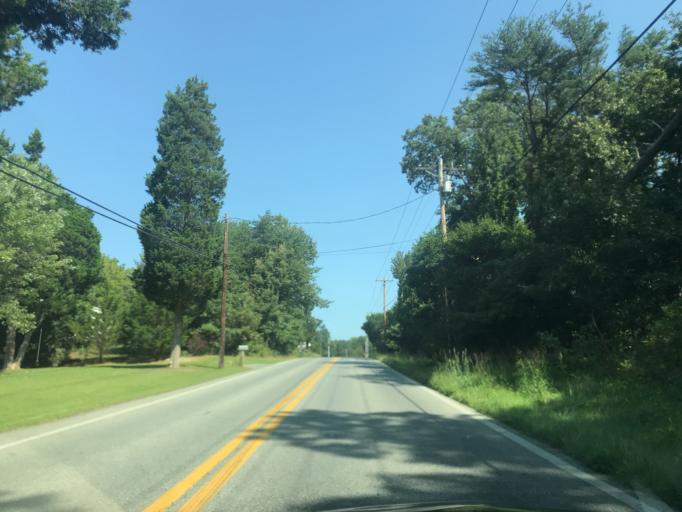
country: US
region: Maryland
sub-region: Calvert County
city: Prince Frederick
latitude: 38.5082
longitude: -76.6222
